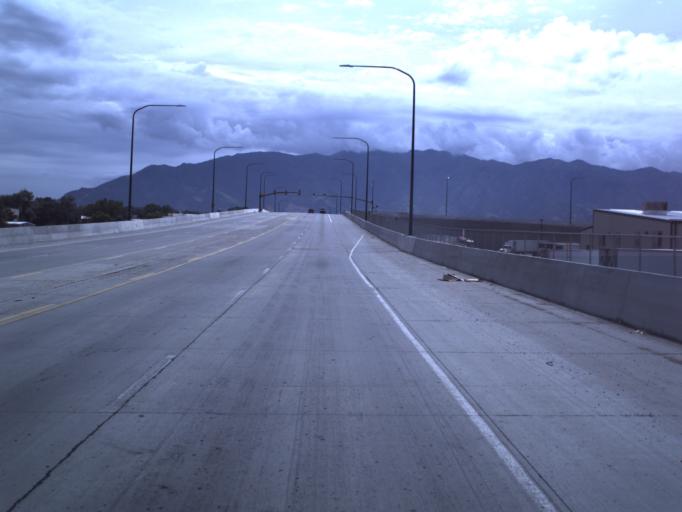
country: US
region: Utah
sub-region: Davis County
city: Clearfield
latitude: 41.1037
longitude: -112.0252
